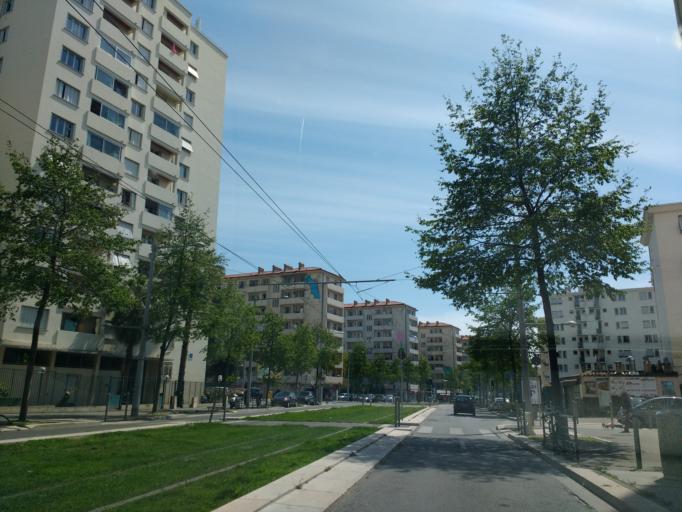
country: FR
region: Provence-Alpes-Cote d'Azur
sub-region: Departement des Alpes-Maritimes
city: Saint-Andre-de-la-Roche
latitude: 43.7165
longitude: 7.2924
